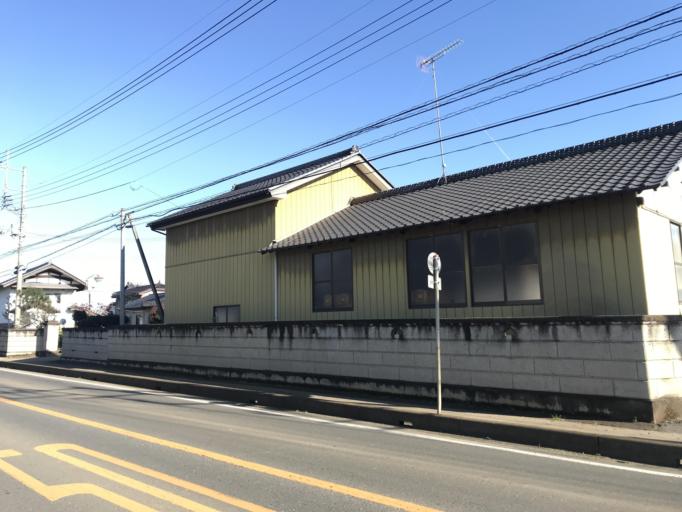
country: JP
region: Tochigi
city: Oyama
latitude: 36.2224
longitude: 139.8240
